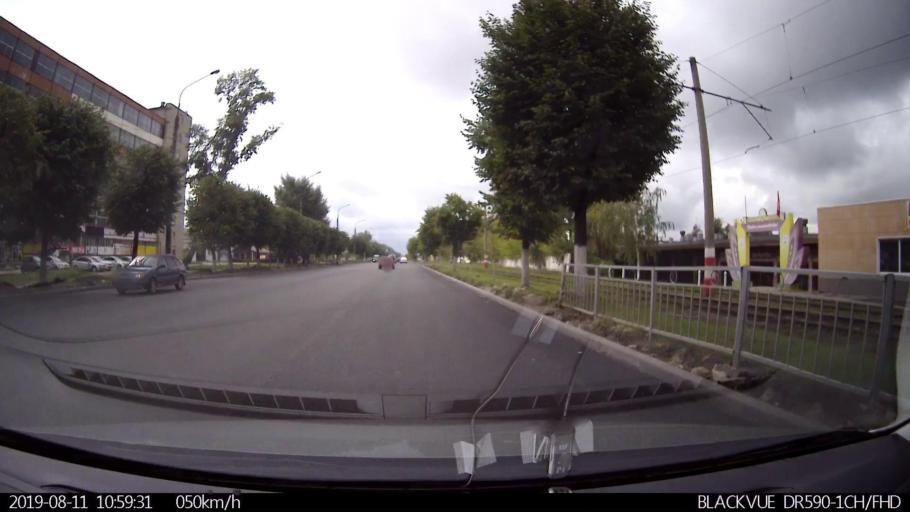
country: RU
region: Ulyanovsk
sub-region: Ulyanovskiy Rayon
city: Ulyanovsk
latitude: 54.2497
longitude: 48.3150
